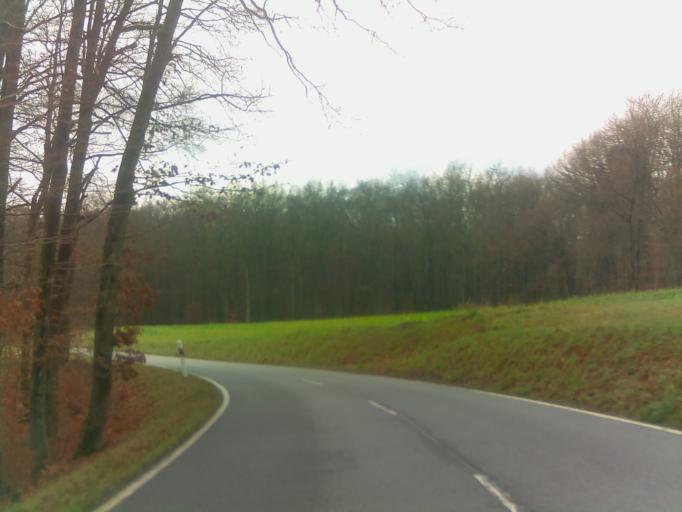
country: DE
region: Baden-Wuerttemberg
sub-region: Karlsruhe Region
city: Wilhelmsfeld
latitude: 49.4912
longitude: 8.7598
